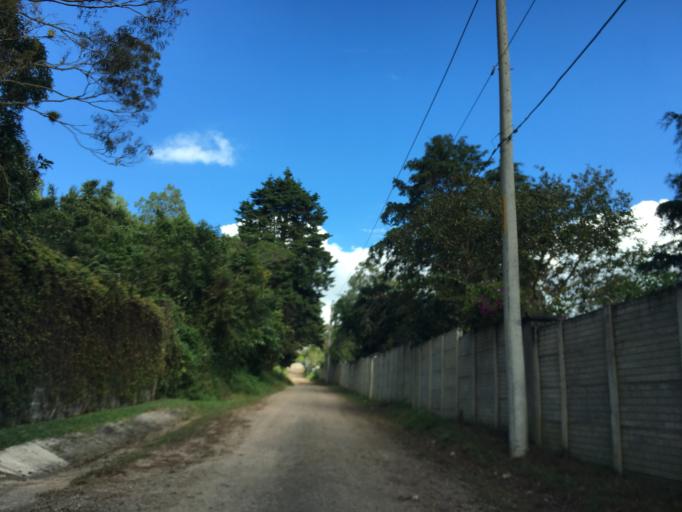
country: GT
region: Guatemala
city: San Jose Pinula
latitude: 14.6051
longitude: -90.4325
